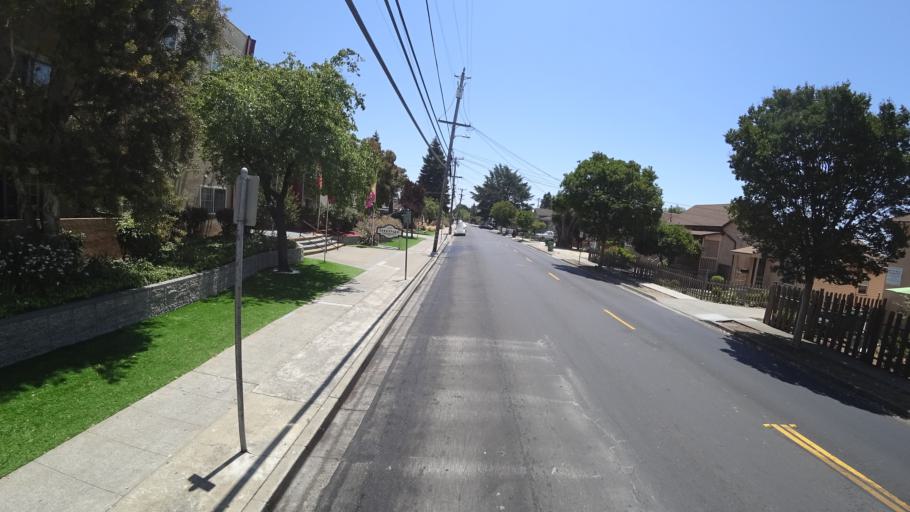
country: US
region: California
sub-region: Alameda County
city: Hayward
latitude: 37.6641
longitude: -122.0825
